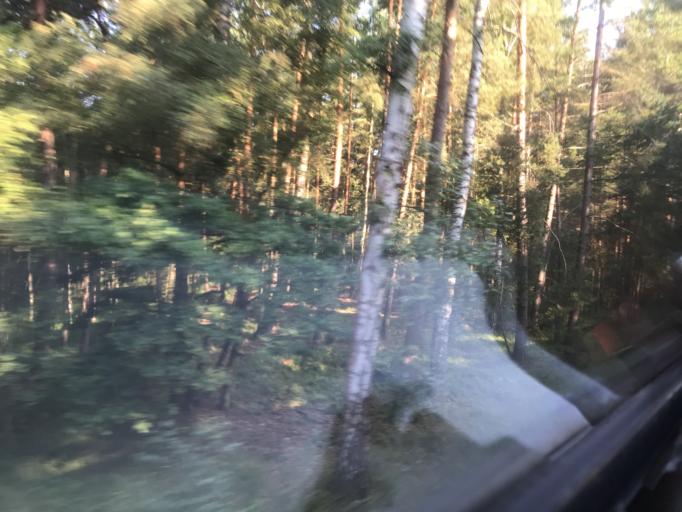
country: CZ
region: Jihocesky
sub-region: Okres Jindrichuv Hradec
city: Lomnice nad Luznici
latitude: 49.1313
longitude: 14.7419
